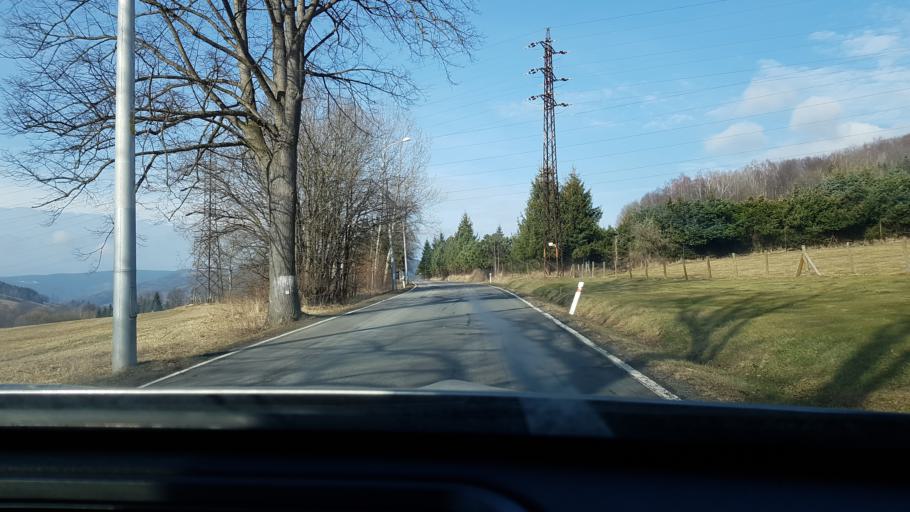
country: CZ
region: Olomoucky
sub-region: Okres Jesenik
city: Jesenik
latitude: 50.2275
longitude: 17.1795
